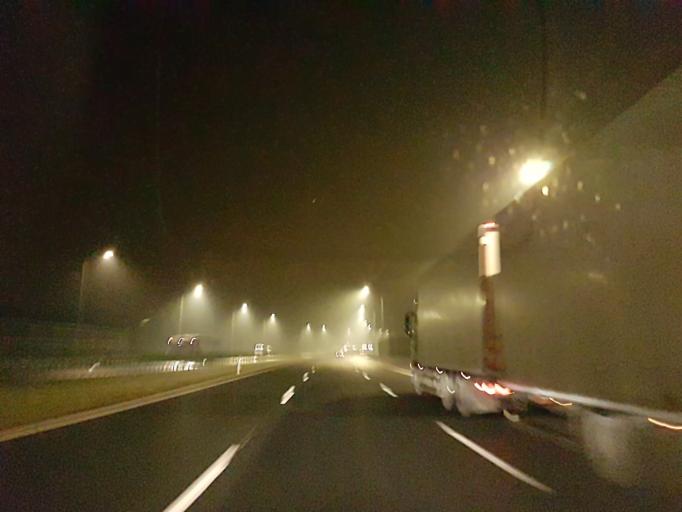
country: PL
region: Masovian Voivodeship
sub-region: Powiat wolominski
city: Marki
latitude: 52.3124
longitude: 21.1248
